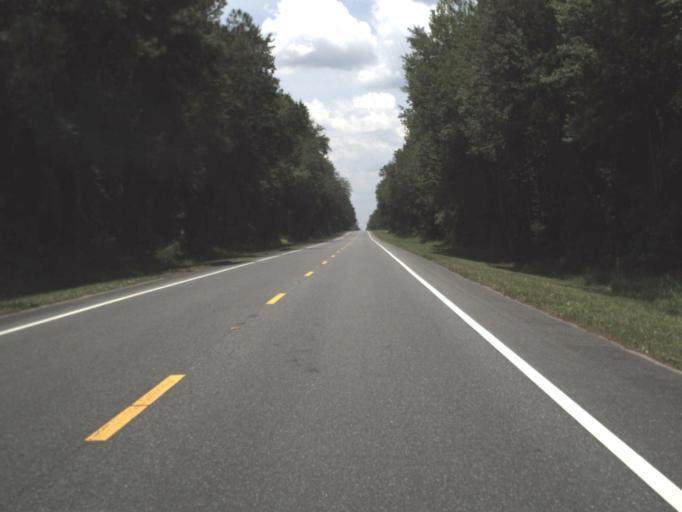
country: US
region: Florida
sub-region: Columbia County
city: Watertown
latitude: 30.1030
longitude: -82.4843
